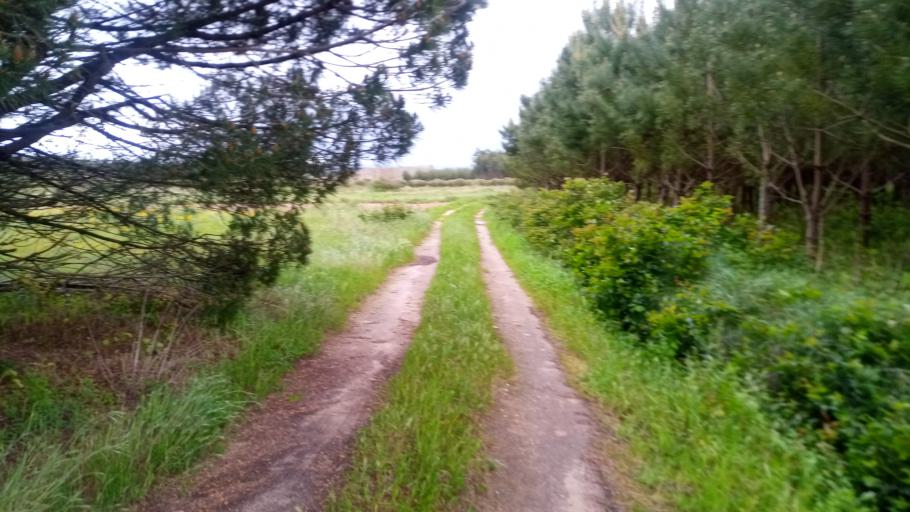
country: PT
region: Leiria
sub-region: Caldas da Rainha
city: Caldas da Rainha
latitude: 39.4486
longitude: -9.1834
